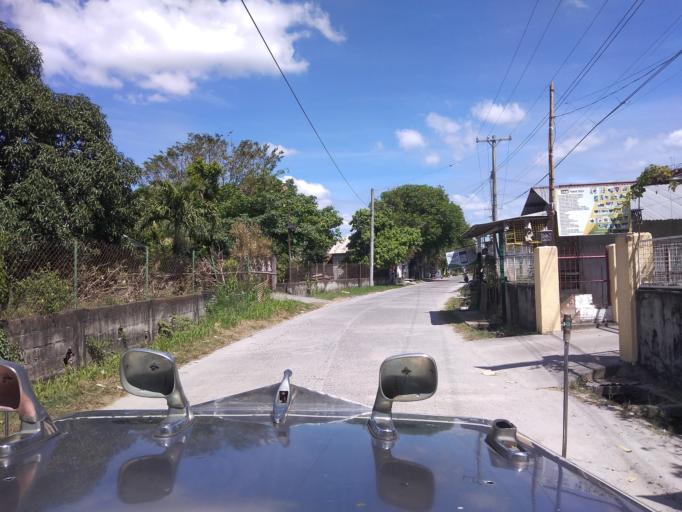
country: PH
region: Central Luzon
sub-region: Province of Pampanga
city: Magliman
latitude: 15.0350
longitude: 120.6484
